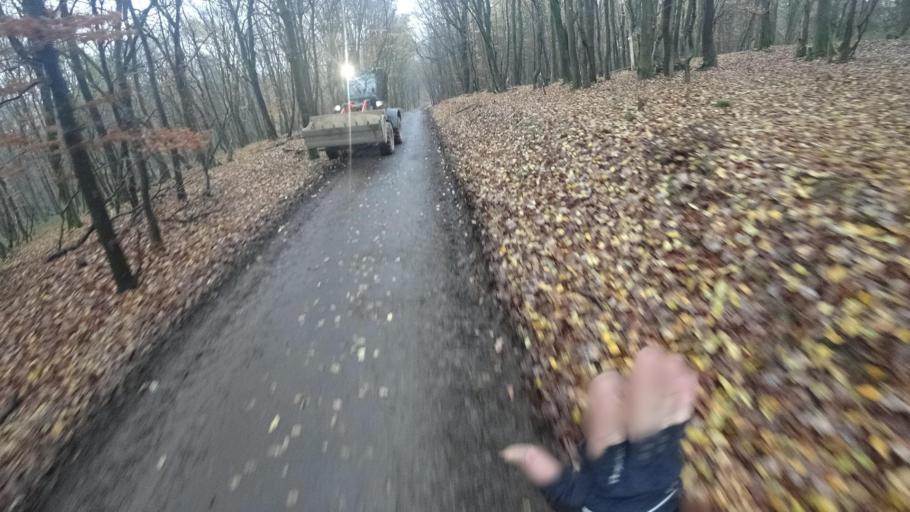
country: DE
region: Rheinland-Pfalz
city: Kesseling
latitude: 50.4977
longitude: 7.0184
